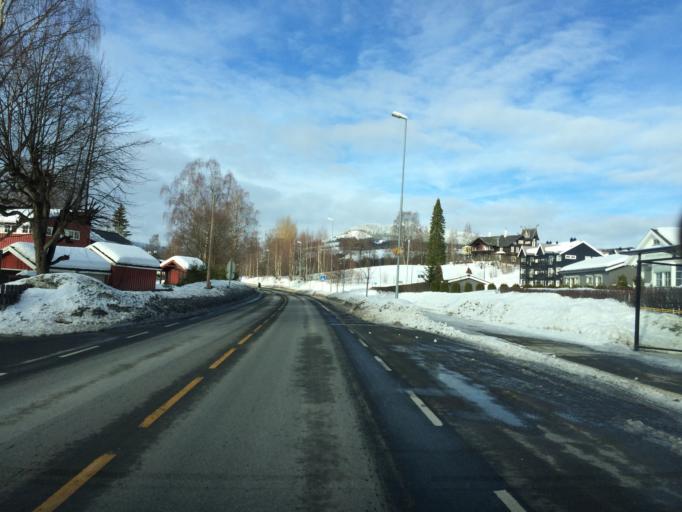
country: NO
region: Oppland
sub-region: Gausdal
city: Segalstad bru
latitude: 61.2137
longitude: 10.2910
